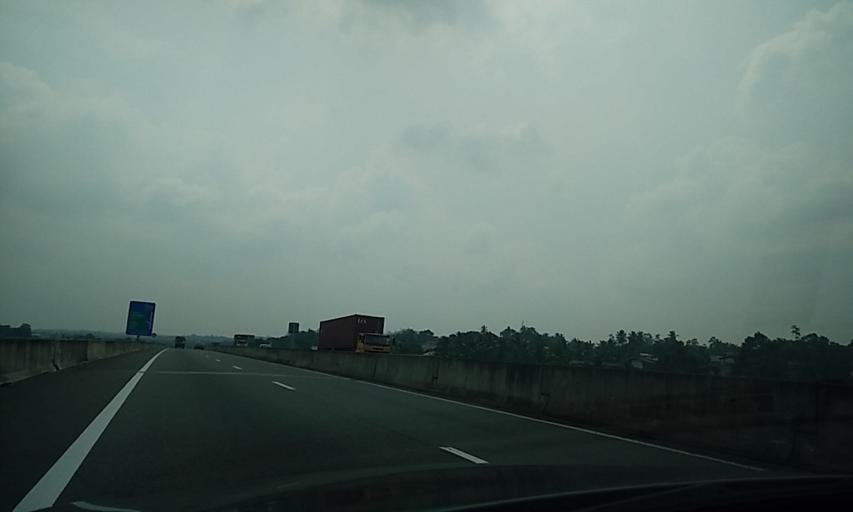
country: LK
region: Western
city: Homagama
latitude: 6.8956
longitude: 79.9787
